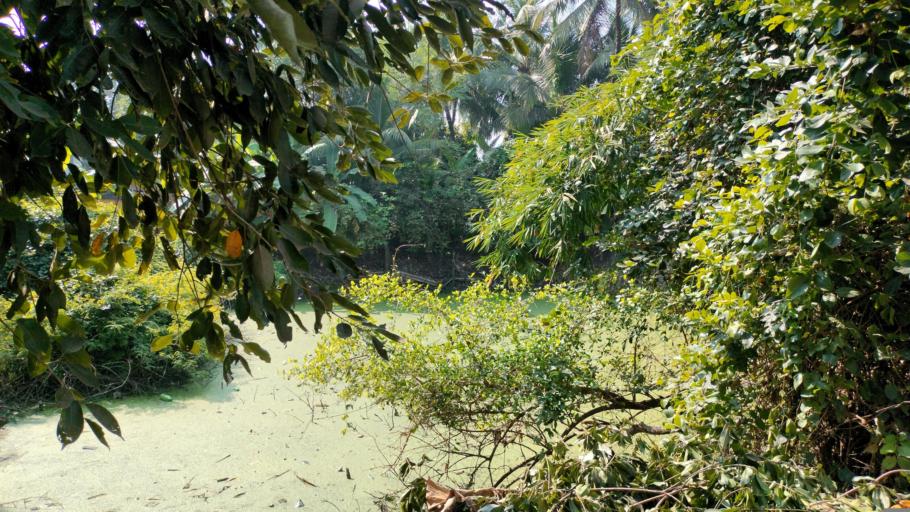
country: IN
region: Maharashtra
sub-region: Thane
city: Virar
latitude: 19.4005
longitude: 72.7896
